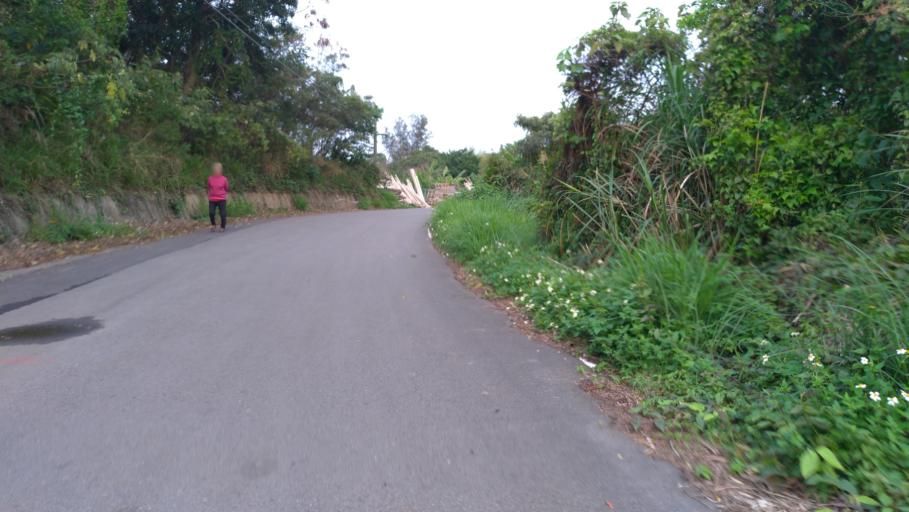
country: TW
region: Taiwan
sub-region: Hsinchu
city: Hsinchu
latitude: 24.7509
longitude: 120.9859
